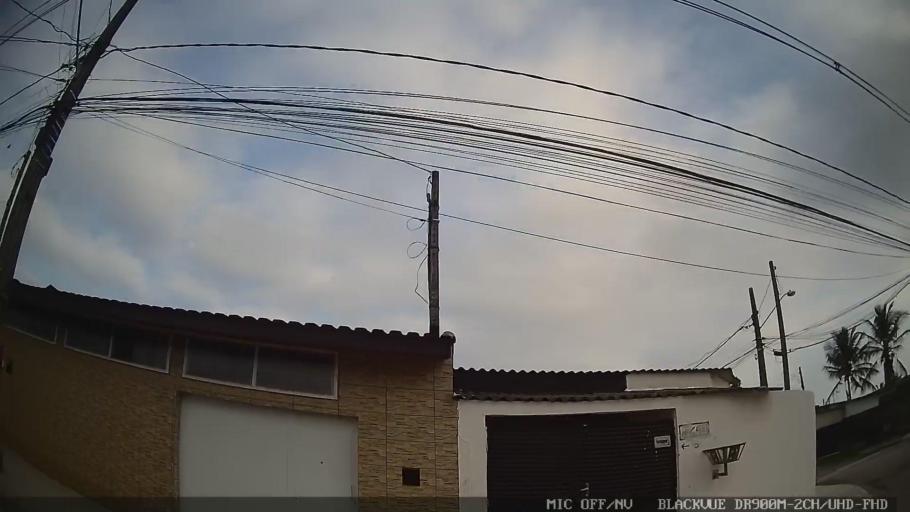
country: BR
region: Sao Paulo
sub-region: Guaruja
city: Guaruja
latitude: -23.9686
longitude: -46.2118
